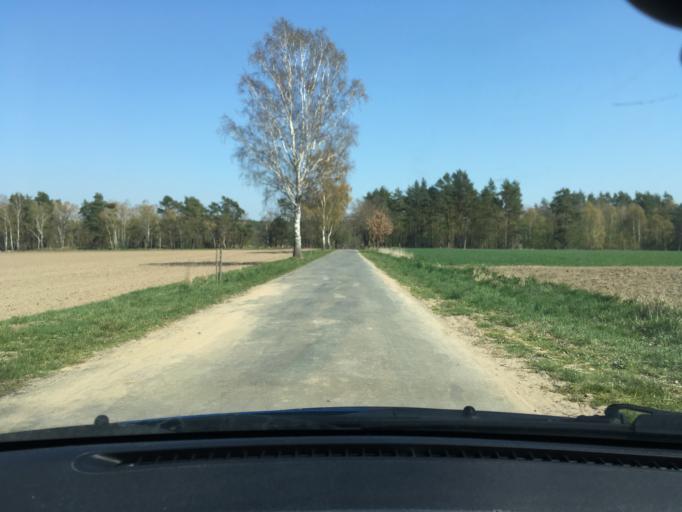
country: DE
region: Lower Saxony
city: Reinstorf
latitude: 53.2004
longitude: 10.6033
